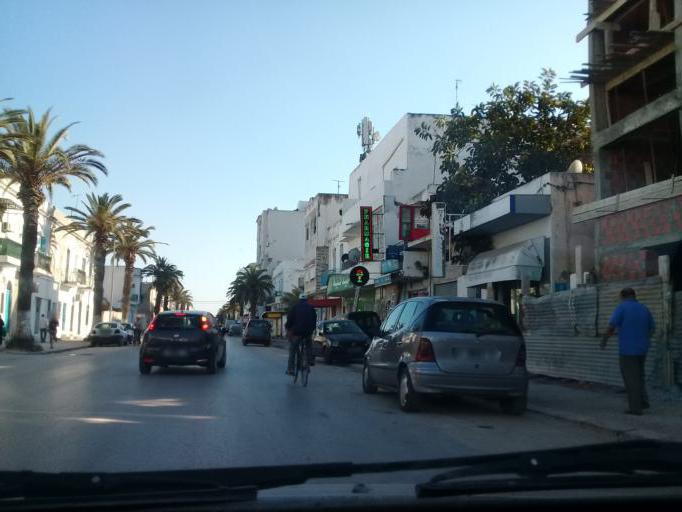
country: TN
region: Tunis
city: La Goulette
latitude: 36.8203
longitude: 10.3073
